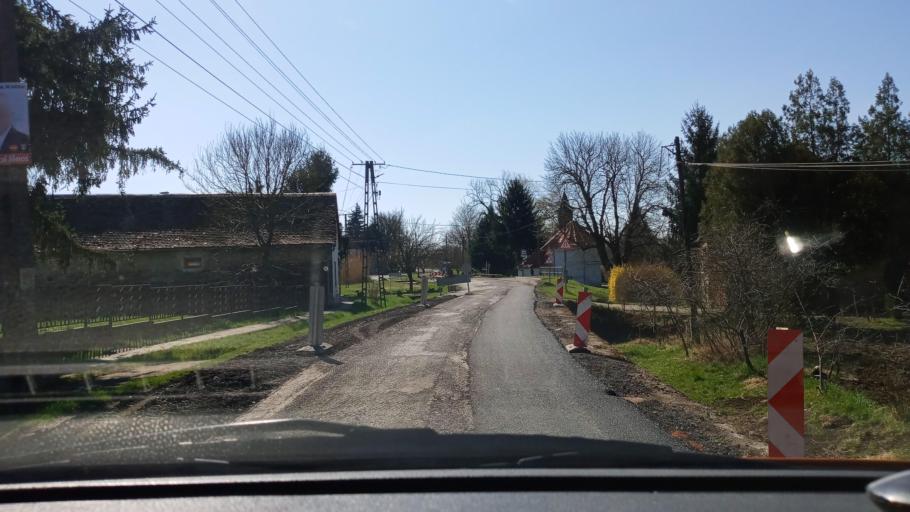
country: HU
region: Baranya
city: Kozarmisleny
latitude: 46.0193
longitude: 18.4078
